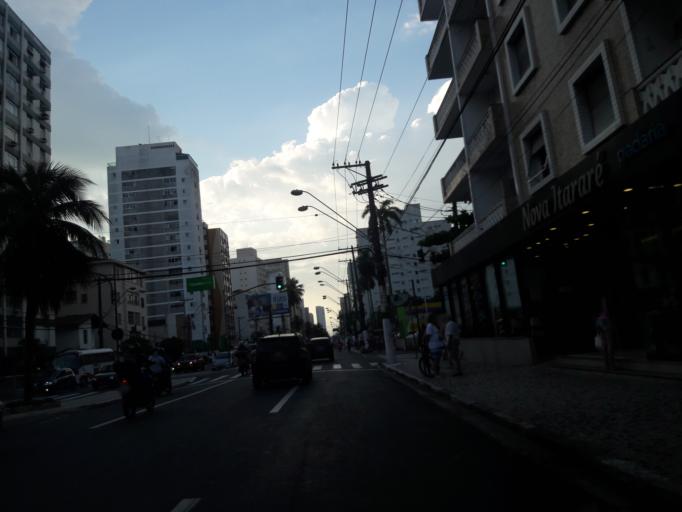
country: BR
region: Sao Paulo
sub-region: Sao Vicente
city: Sao Vicente
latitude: -23.9715
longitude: -46.3703
